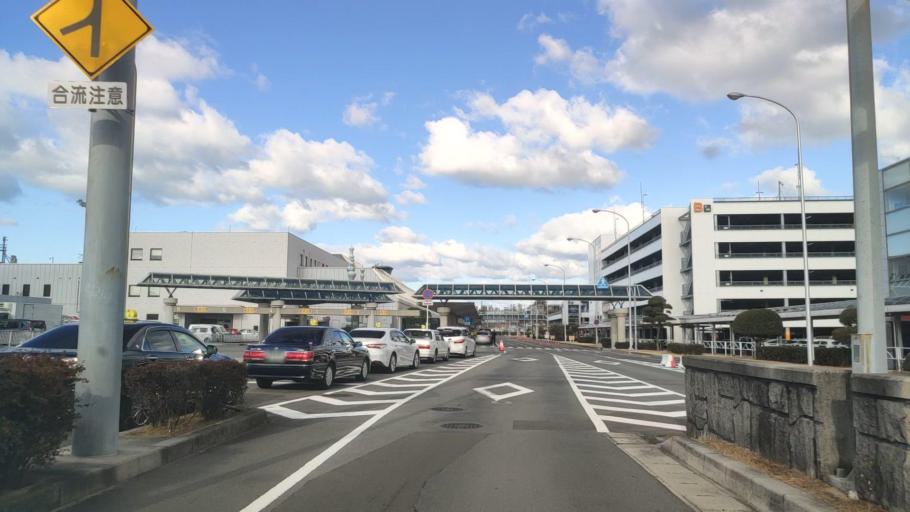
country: JP
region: Ehime
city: Masaki-cho
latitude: 33.8283
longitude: 132.7059
